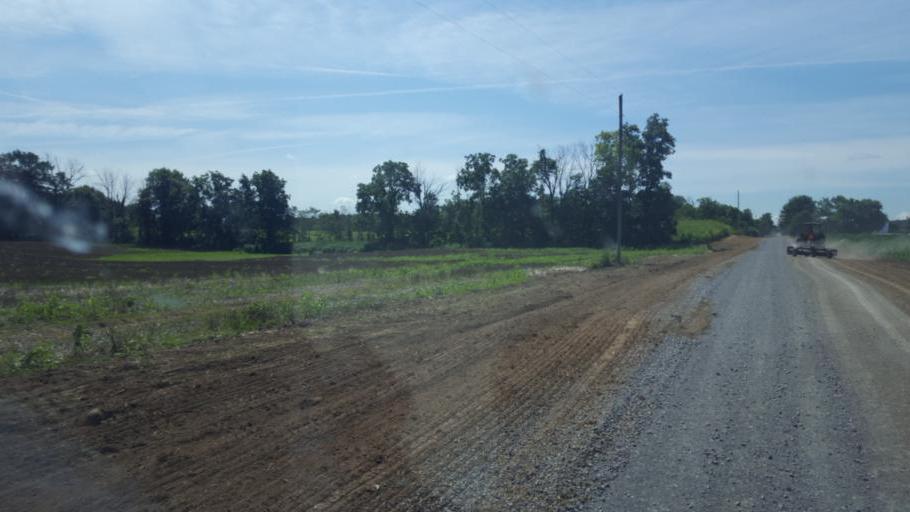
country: US
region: Ohio
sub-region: Knox County
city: Centerburg
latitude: 40.4452
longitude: -82.7172
